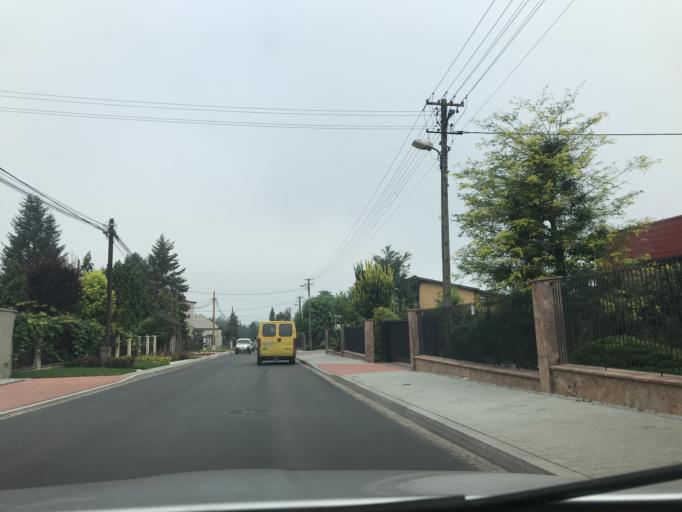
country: PL
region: Lesser Poland Voivodeship
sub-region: Powiat krakowski
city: Ochojno
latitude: 50.0066
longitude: 19.9796
